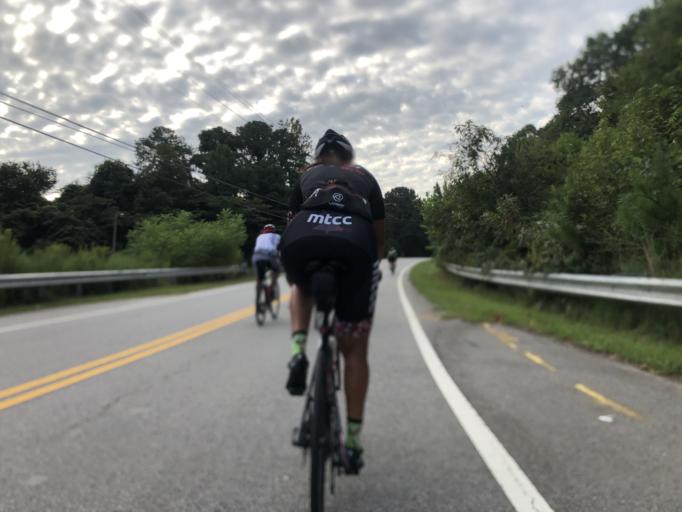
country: US
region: Georgia
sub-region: Fulton County
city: Palmetto
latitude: 33.6175
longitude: -84.6705
